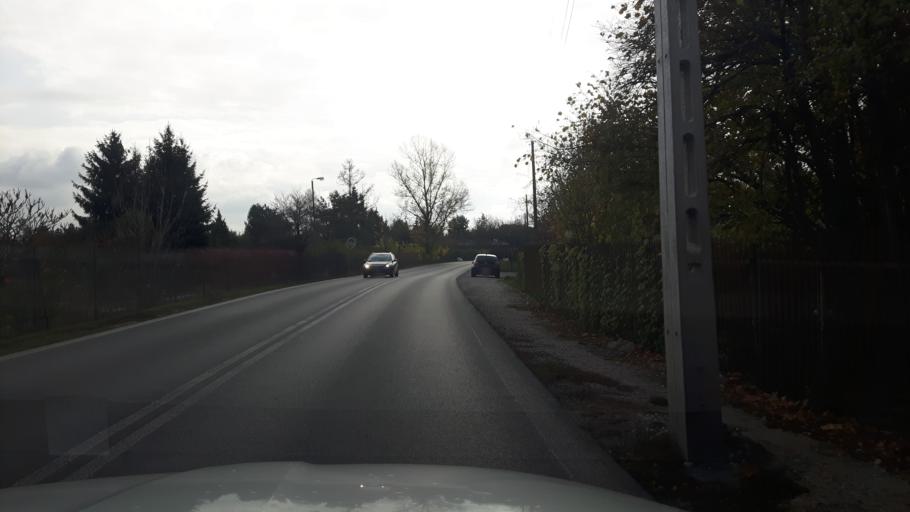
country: PL
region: Masovian Voivodeship
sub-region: Powiat wolominski
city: Zabki
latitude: 52.2810
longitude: 21.0962
